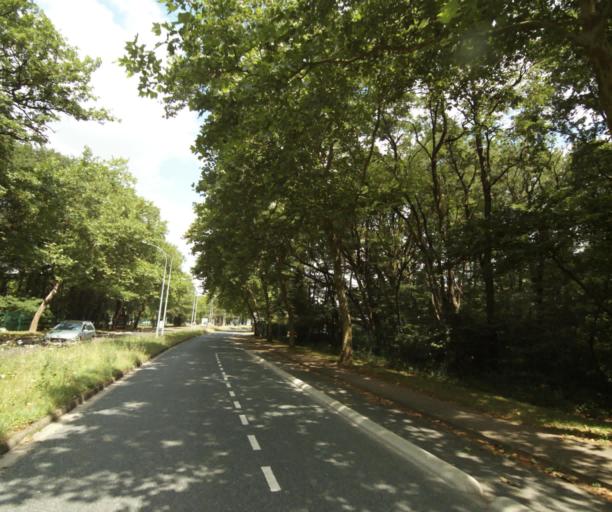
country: FR
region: Centre
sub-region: Departement du Loiret
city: Saint-Cyr-en-Val
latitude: 47.8270
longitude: 1.9370
